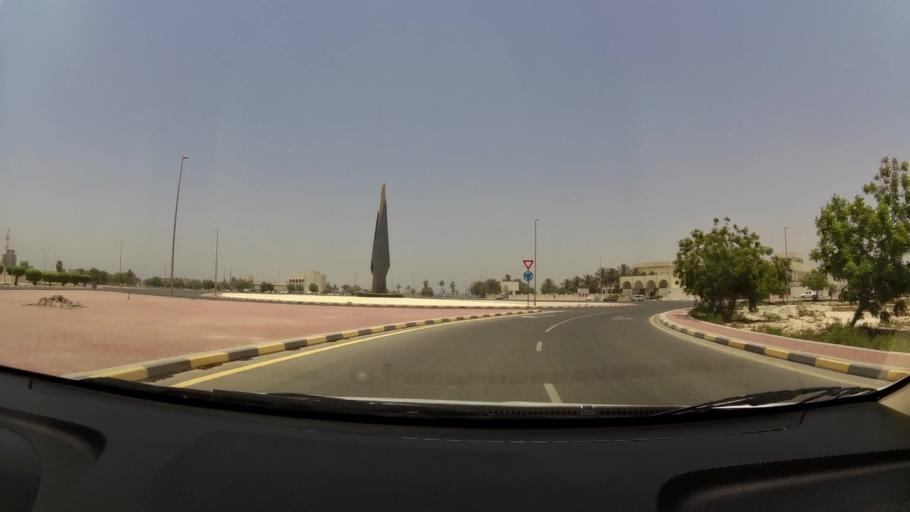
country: AE
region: Umm al Qaywayn
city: Umm al Qaywayn
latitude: 25.5717
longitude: 55.5646
